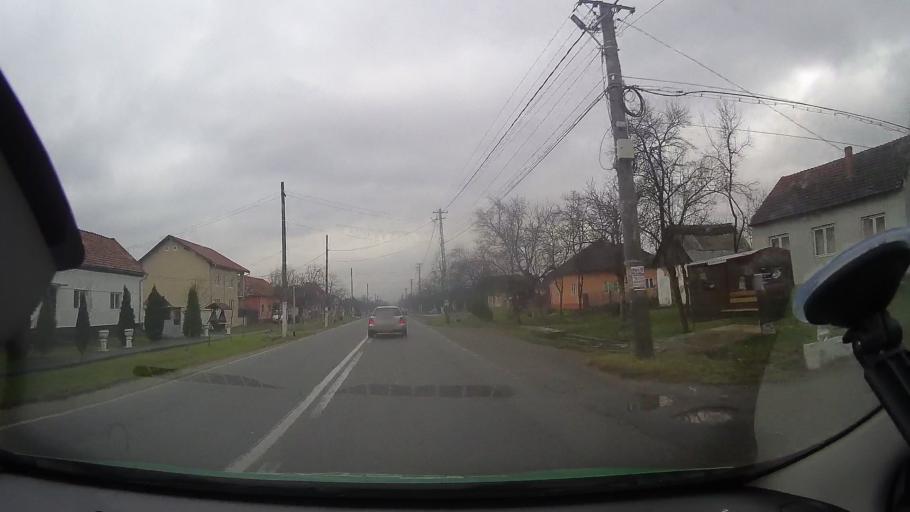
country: RO
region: Arad
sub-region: Comuna Almas
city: Almas
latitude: 46.2843
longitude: 22.2552
